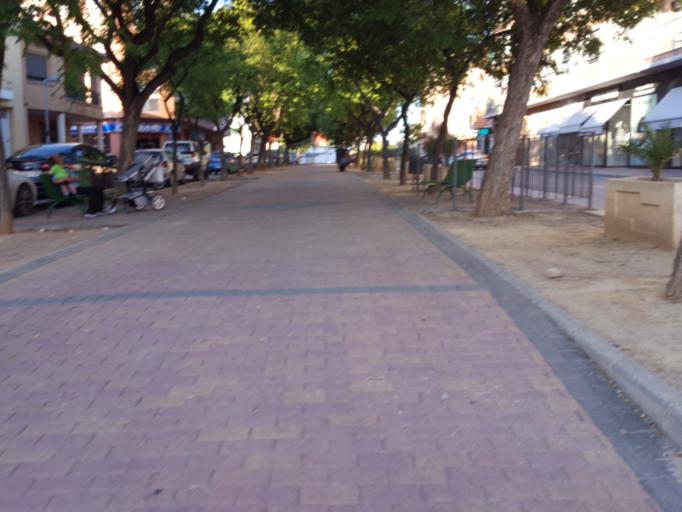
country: ES
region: Murcia
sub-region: Murcia
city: Murcia
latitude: 37.9970
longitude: -1.1749
